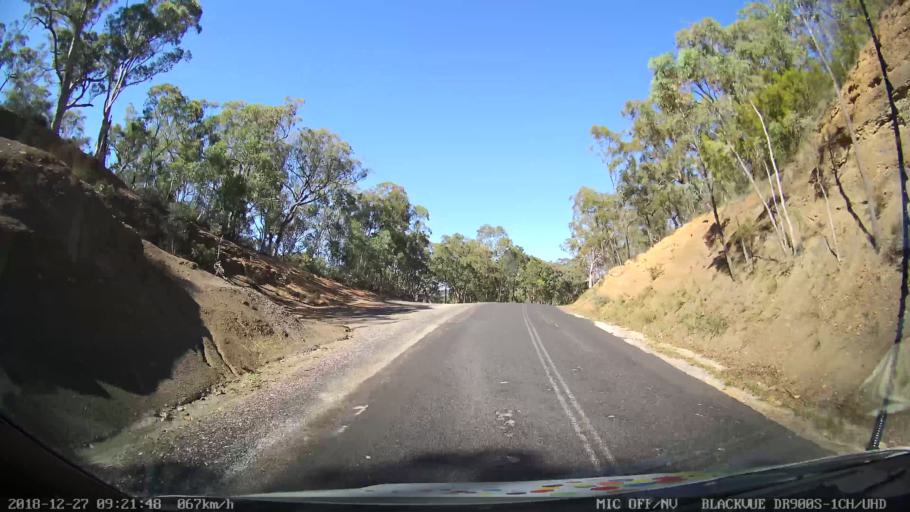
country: AU
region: New South Wales
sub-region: Lithgow
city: Portland
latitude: -33.1276
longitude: 150.0147
